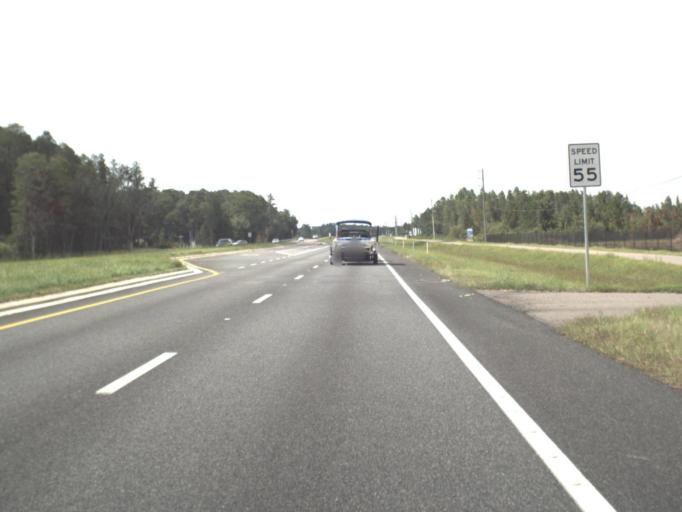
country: US
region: Florida
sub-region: Pasco County
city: Land O' Lakes
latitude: 28.2835
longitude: -82.4858
